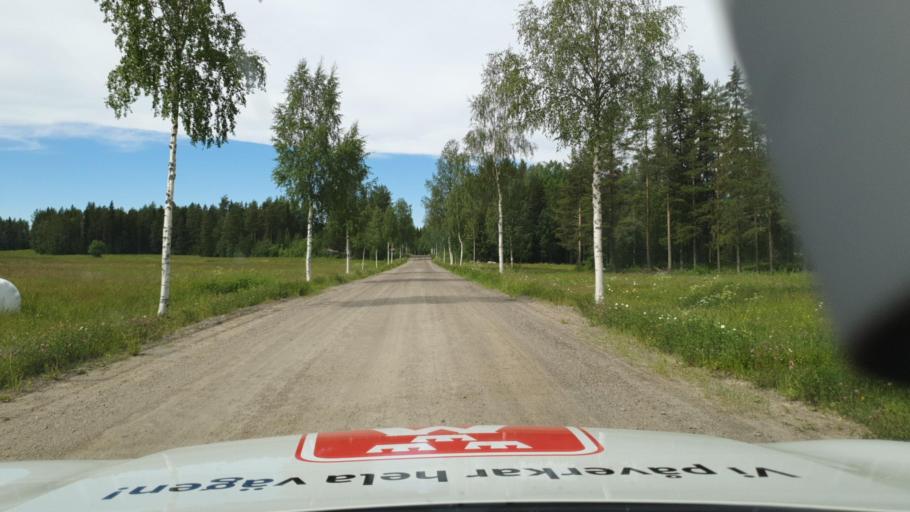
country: SE
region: Vaesterbotten
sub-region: Skelleftea Kommun
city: Burtraesk
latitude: 64.4574
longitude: 20.4749
